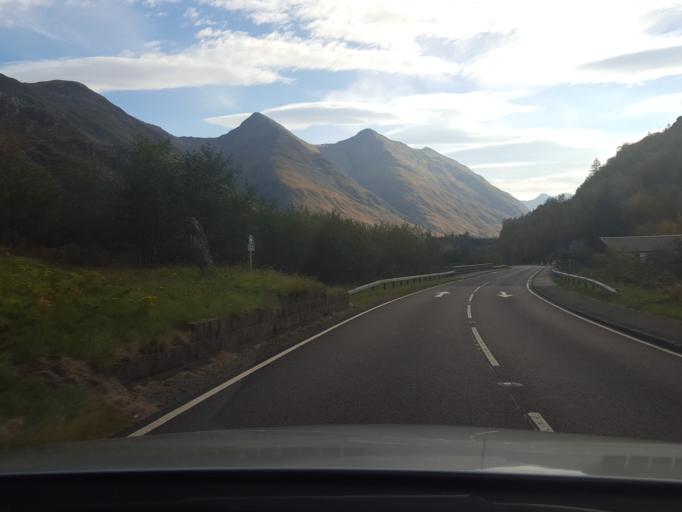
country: GB
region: Scotland
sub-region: Highland
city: Fort William
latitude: 57.2134
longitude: -5.4155
